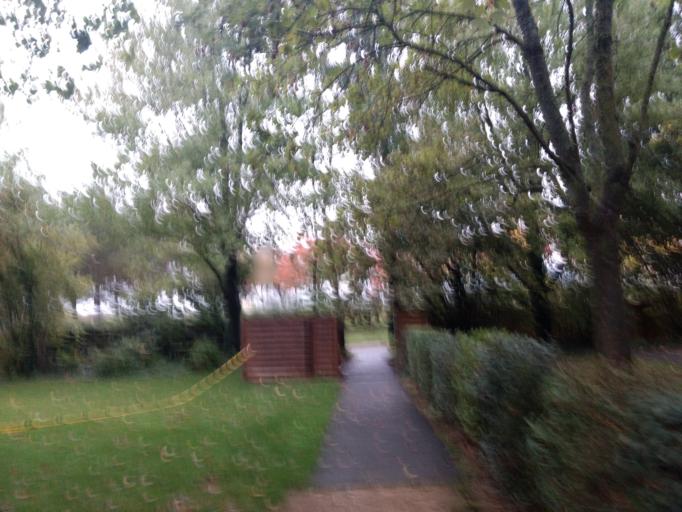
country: FR
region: Poitou-Charentes
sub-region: Departement de la Vienne
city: Jaunay-Clan
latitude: 46.6712
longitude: 0.3681
